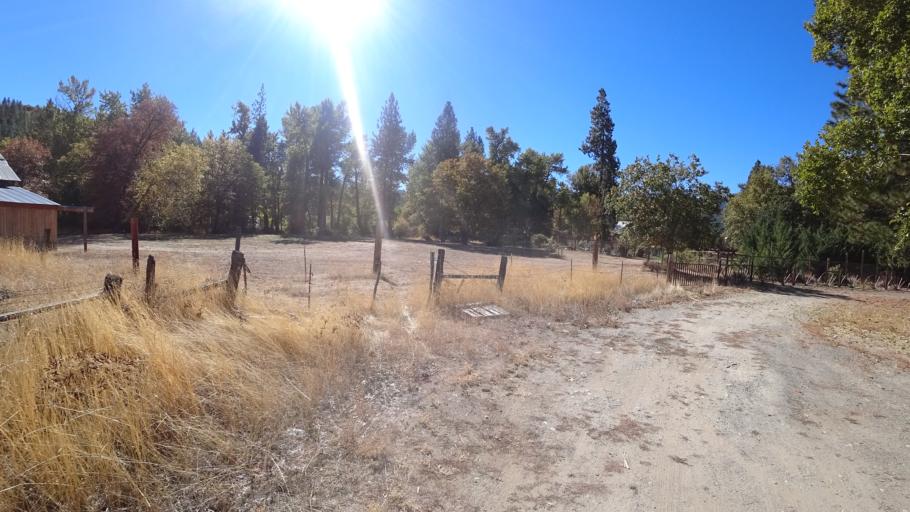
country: US
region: California
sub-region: Siskiyou County
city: Yreka
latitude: 41.4539
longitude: -122.8852
